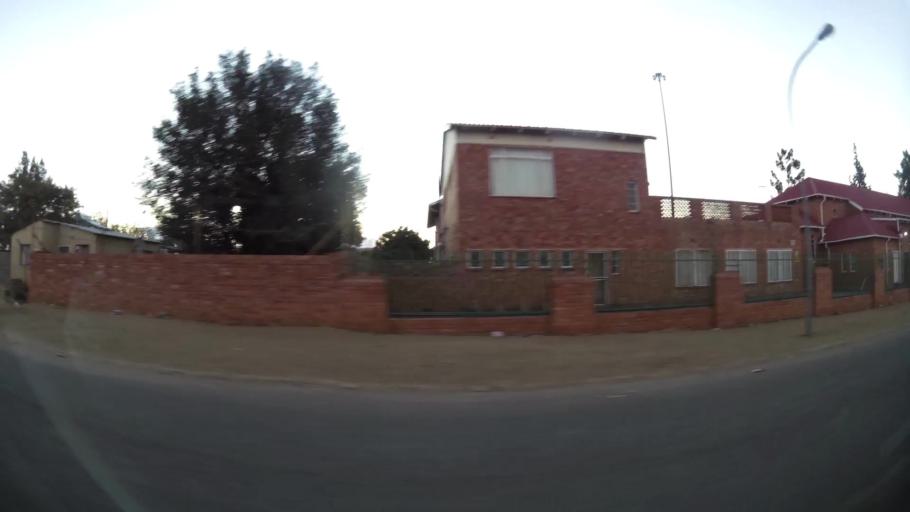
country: ZA
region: Northern Cape
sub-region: Frances Baard District Municipality
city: Kimberley
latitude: -28.7154
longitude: 24.7679
